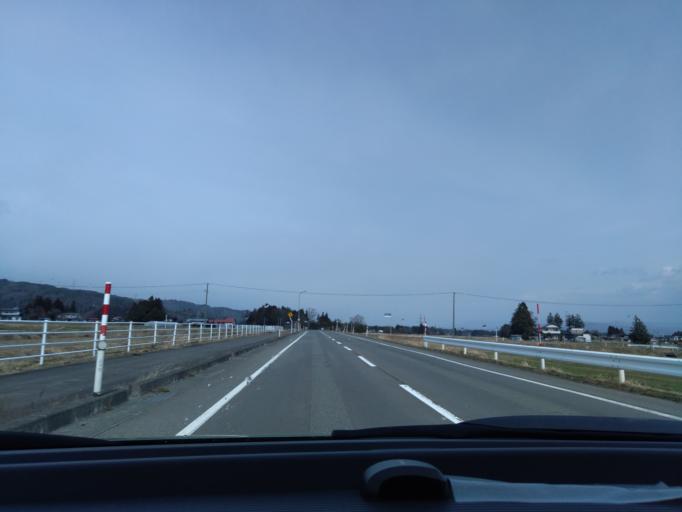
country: JP
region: Iwate
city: Morioka-shi
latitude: 39.5767
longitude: 141.1101
